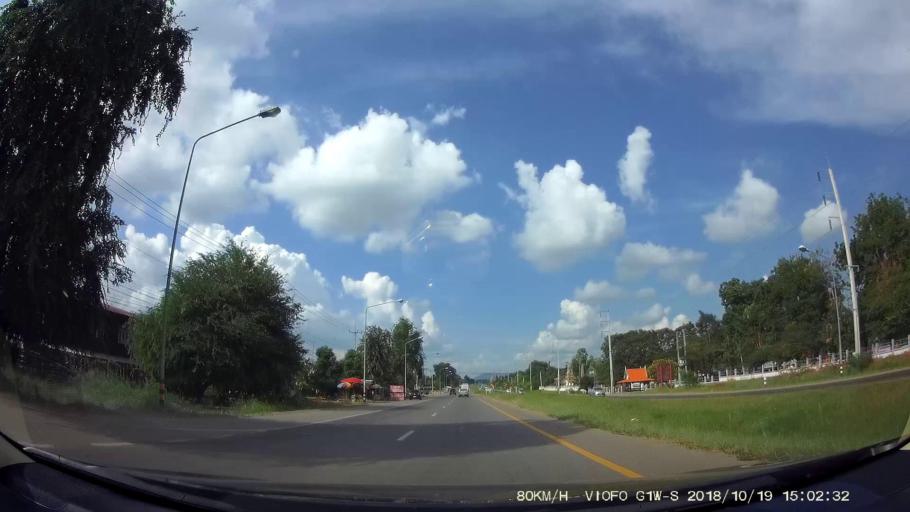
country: TH
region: Chaiyaphum
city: Phu Khiao
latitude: 16.3999
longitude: 102.1310
